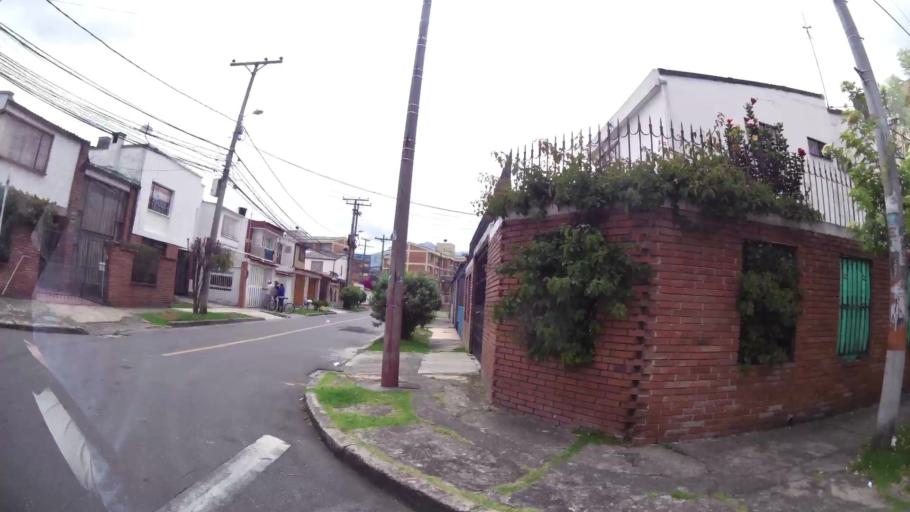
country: CO
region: Bogota D.C.
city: Barrio San Luis
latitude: 4.6848
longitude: -74.0689
